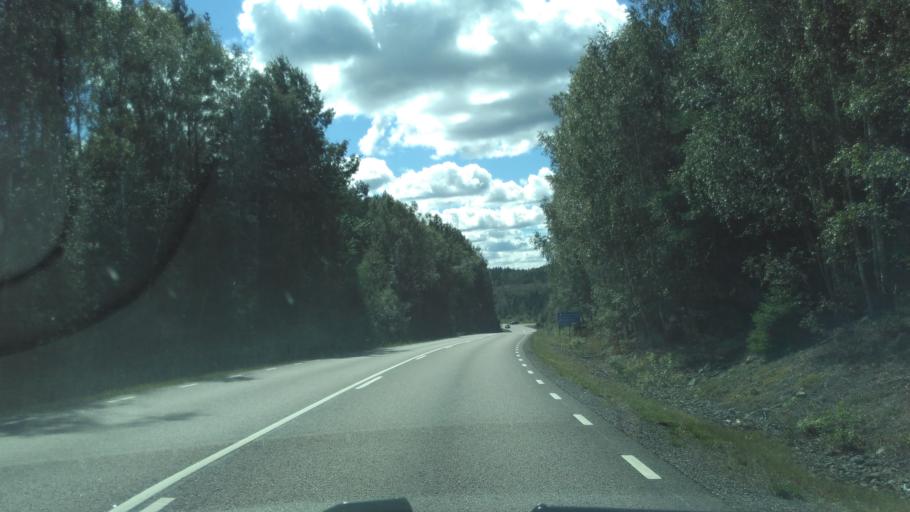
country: SE
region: Vaestra Goetaland
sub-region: Harryda Kommun
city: Ravlanda
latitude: 57.6710
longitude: 12.4920
